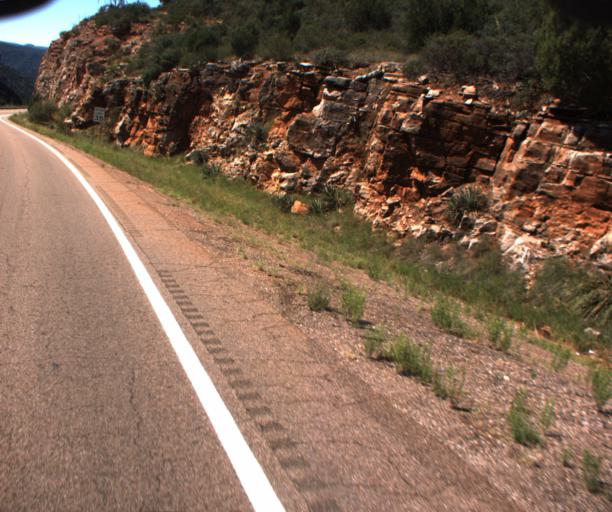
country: US
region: Arizona
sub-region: Navajo County
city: Cibecue
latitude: 33.8240
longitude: -110.4627
